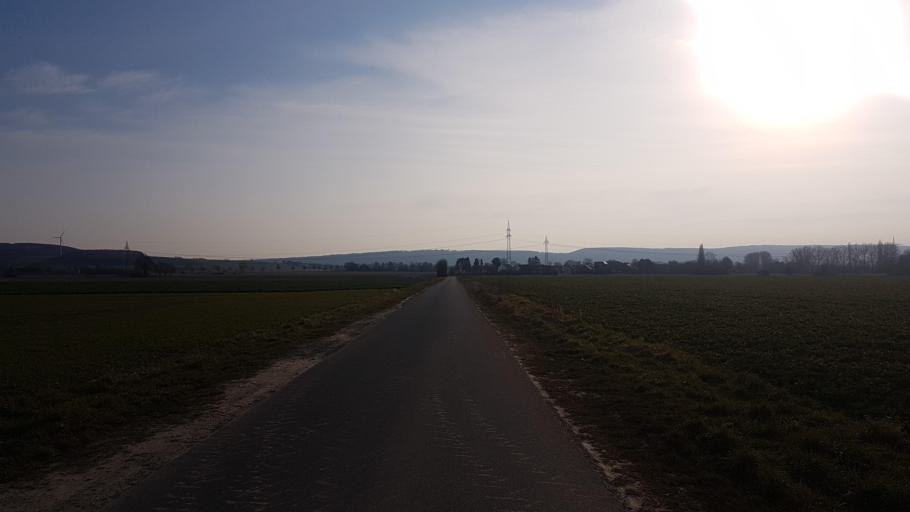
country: DE
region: Lower Saxony
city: Ronnenberg
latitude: 52.2886
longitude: 9.6587
